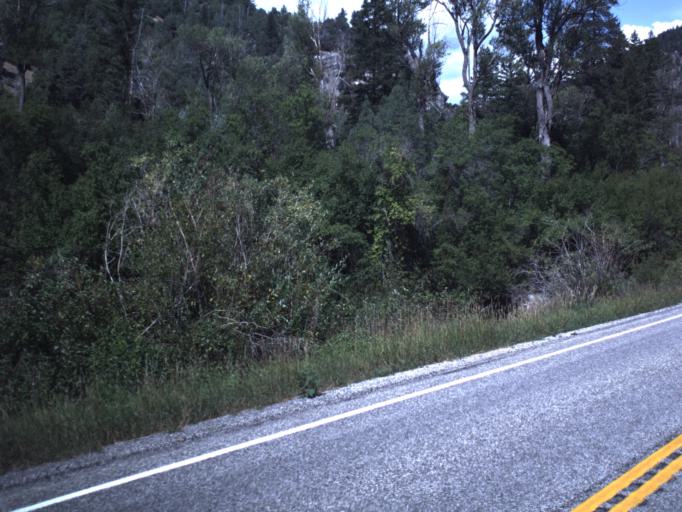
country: US
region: Utah
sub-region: Cache County
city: North Logan
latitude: 41.7987
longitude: -111.6406
